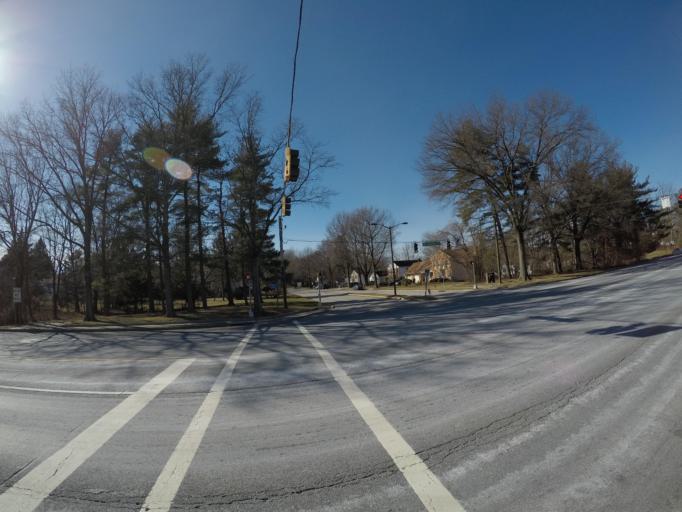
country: US
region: Maryland
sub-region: Howard County
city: Columbia
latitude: 39.2348
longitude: -76.8307
